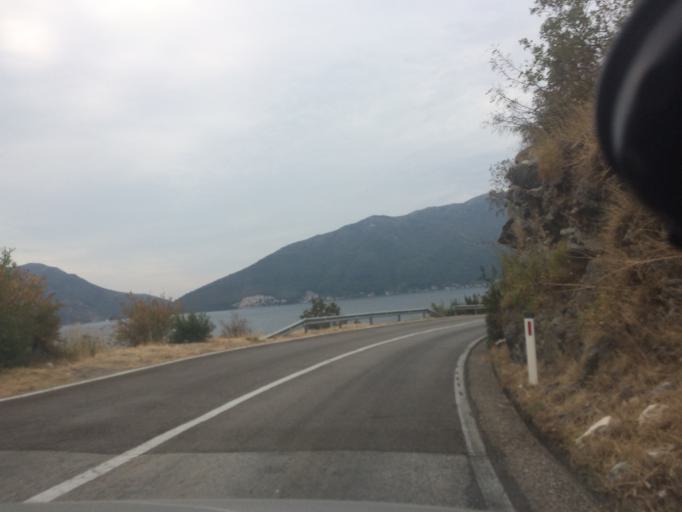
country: ME
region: Kotor
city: Risan
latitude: 42.5123
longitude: 18.6814
